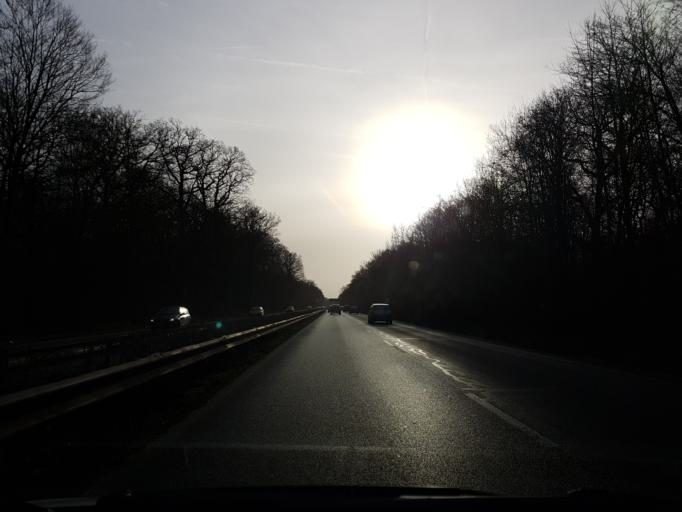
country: FR
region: Ile-de-France
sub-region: Departement de l'Essonne
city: Quincy-sous-Senart
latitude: 48.6549
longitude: 2.5245
